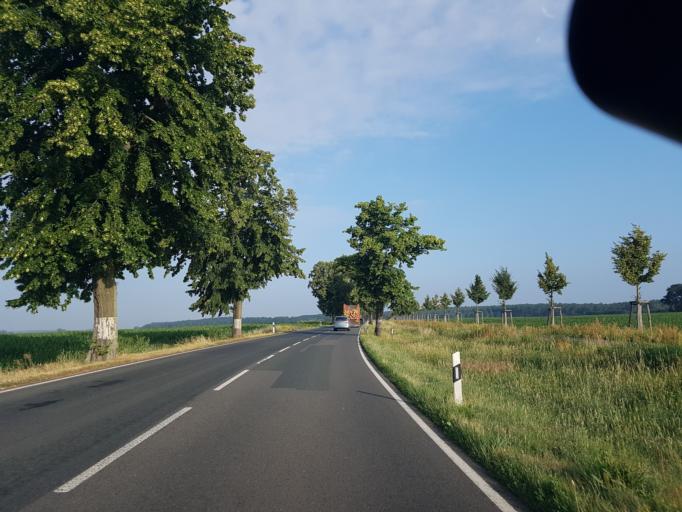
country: DE
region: Brandenburg
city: Schlieben
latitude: 51.7316
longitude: 13.3562
